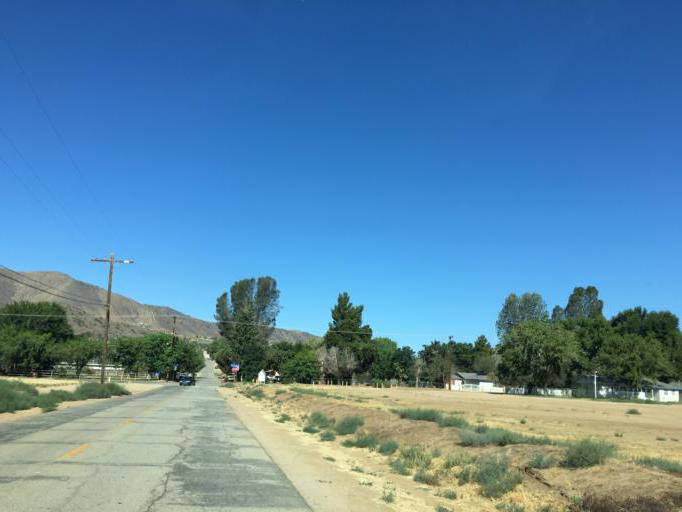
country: US
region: California
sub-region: Los Angeles County
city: Acton
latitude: 34.4699
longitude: -118.1960
